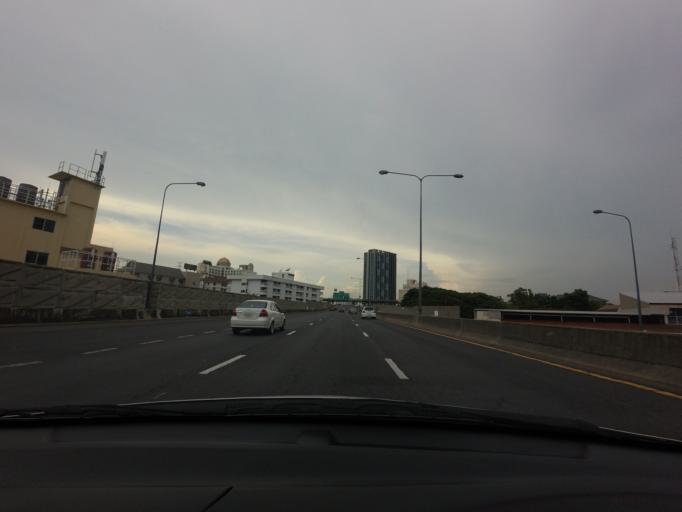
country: TH
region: Bangkok
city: Watthana
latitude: 13.7438
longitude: 100.6051
